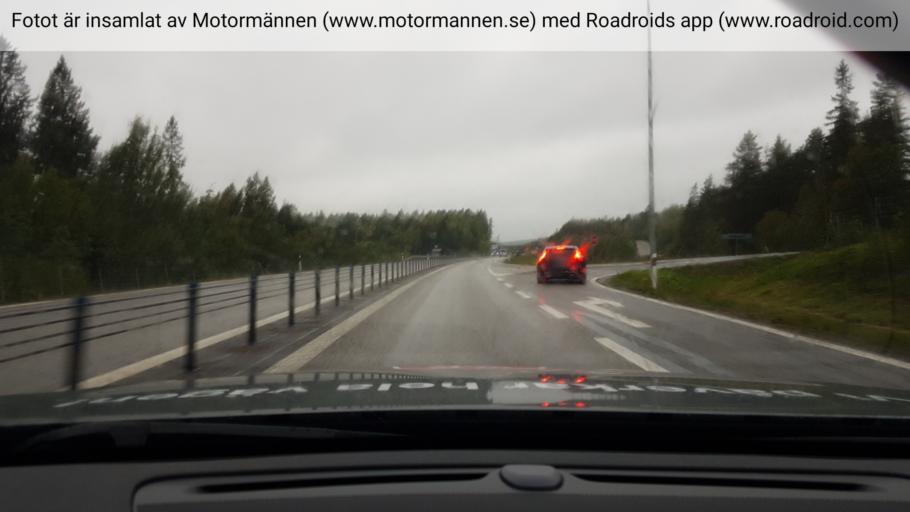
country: SE
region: OErebro
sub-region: Karlskoga Kommun
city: Karlskoga
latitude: 59.3232
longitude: 14.4536
